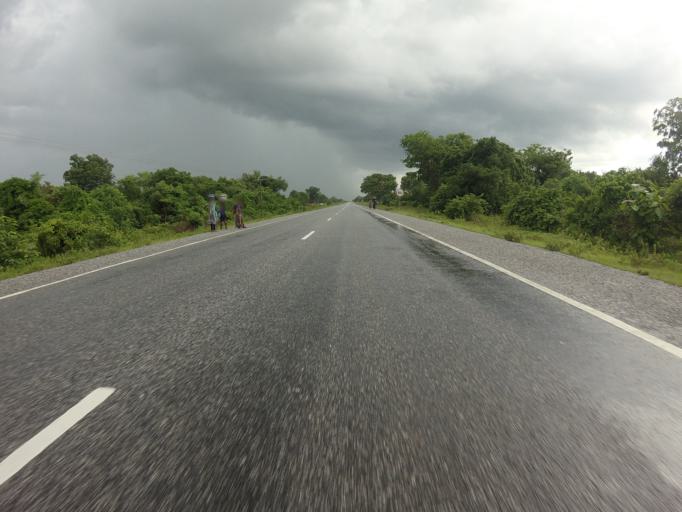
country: GH
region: Northern
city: Tamale
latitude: 9.1501
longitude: -1.5423
